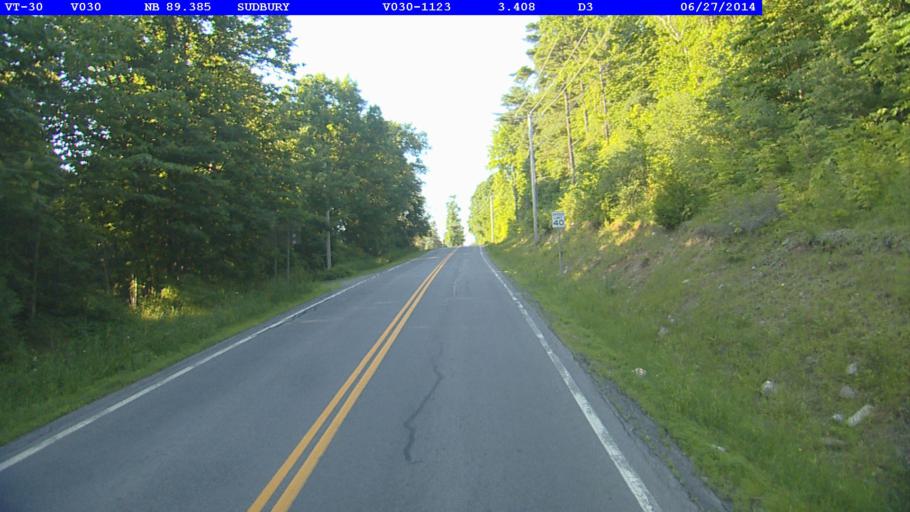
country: US
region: Vermont
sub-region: Rutland County
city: Brandon
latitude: 43.7970
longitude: -73.2054
